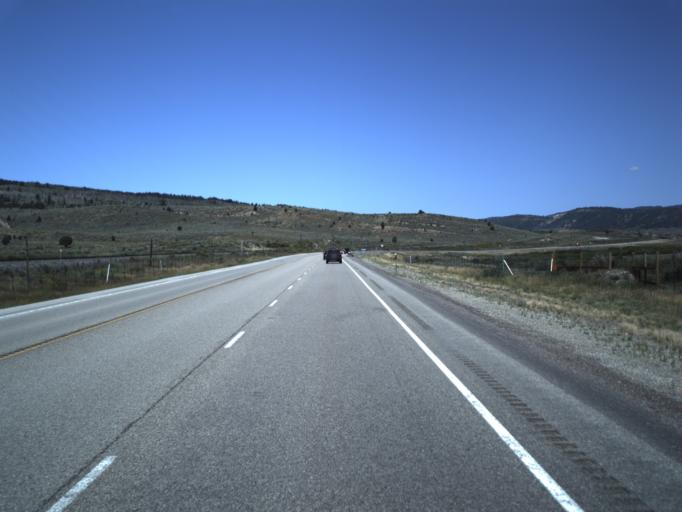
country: US
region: Utah
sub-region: Carbon County
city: Helper
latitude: 39.8818
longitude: -111.0449
